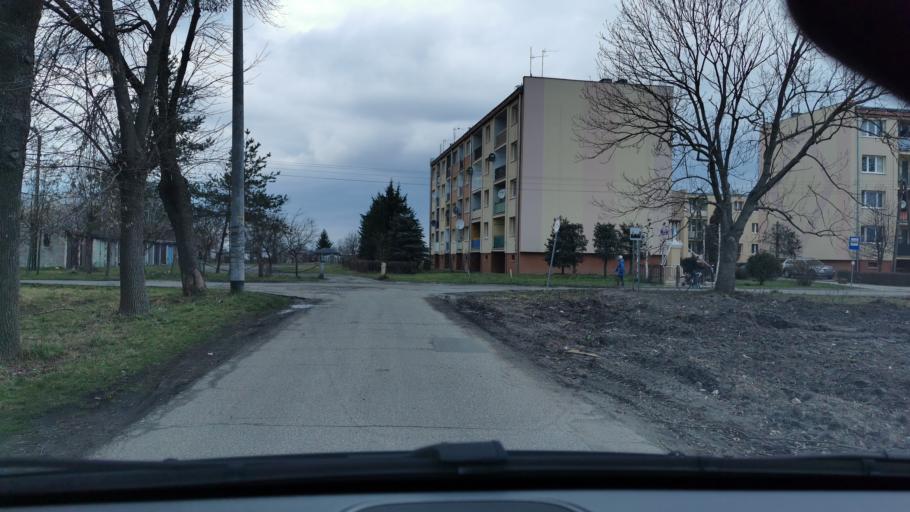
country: PL
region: Masovian Voivodeship
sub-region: Powiat zyrardowski
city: Guzow
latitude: 52.1152
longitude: 20.3268
